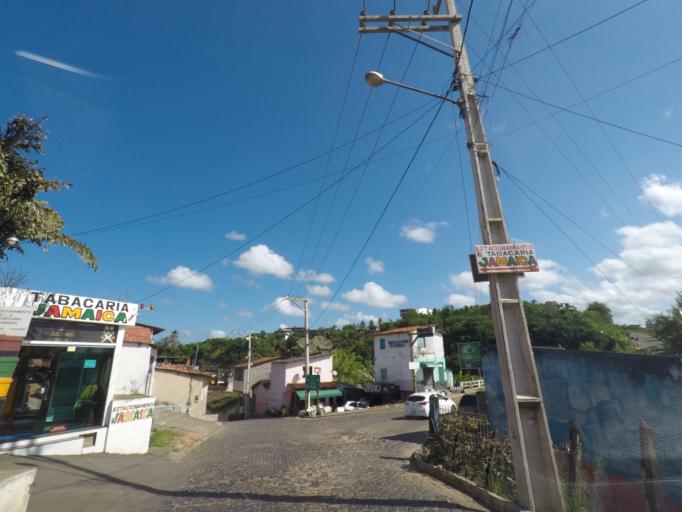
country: BR
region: Bahia
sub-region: Camamu
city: Camamu
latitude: -13.9477
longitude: -39.1070
